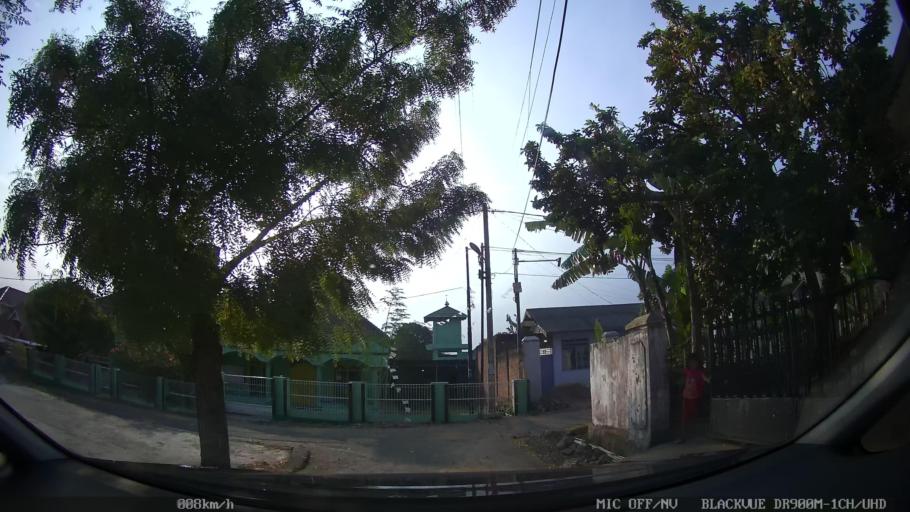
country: ID
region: Lampung
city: Kedaton
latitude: -5.3981
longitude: 105.2988
